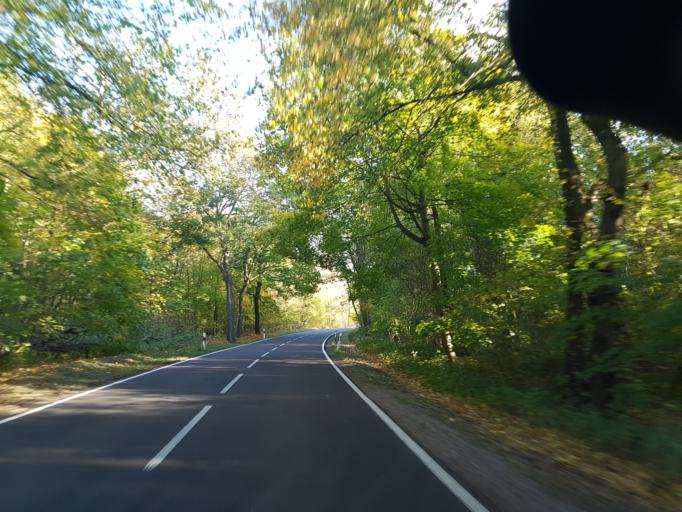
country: DE
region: Brandenburg
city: Brieselang
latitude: 52.6230
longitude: 12.9530
